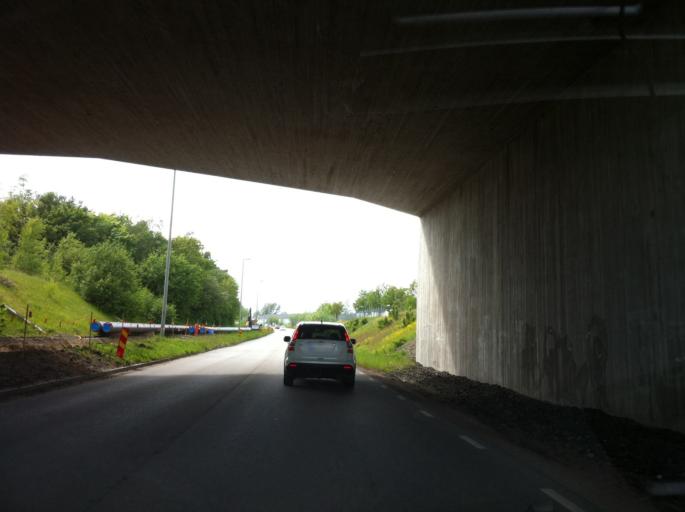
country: SE
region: Skane
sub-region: Landskrona
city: Landskrona
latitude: 55.8649
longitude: 12.8814
